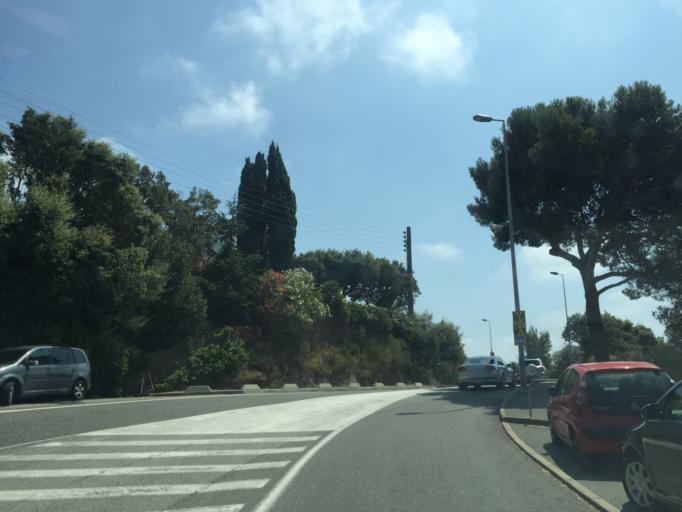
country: FR
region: Provence-Alpes-Cote d'Azur
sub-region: Departement du Var
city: Saint-Raphael
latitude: 43.4284
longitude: 6.8715
